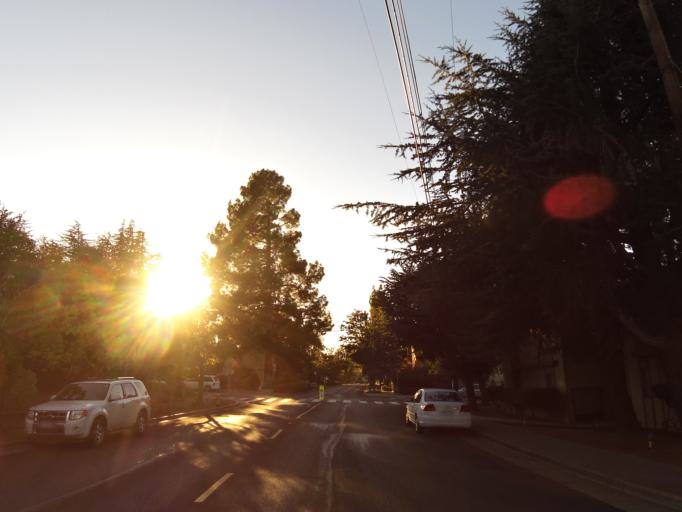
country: US
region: California
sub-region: Santa Clara County
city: Los Altos
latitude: 37.3740
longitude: -122.1101
